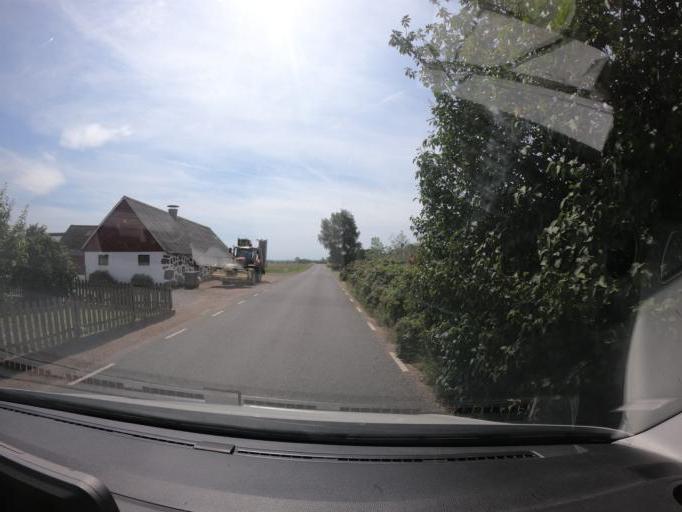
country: SE
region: Skane
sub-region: Angelholms Kommun
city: Vejbystrand
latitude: 56.4017
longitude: 12.7022
